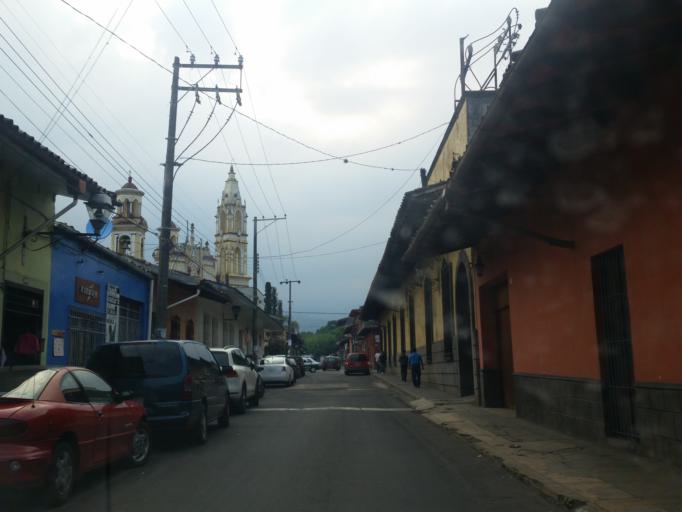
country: MX
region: Veracruz
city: Coatepec
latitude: 19.4522
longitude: -96.9564
